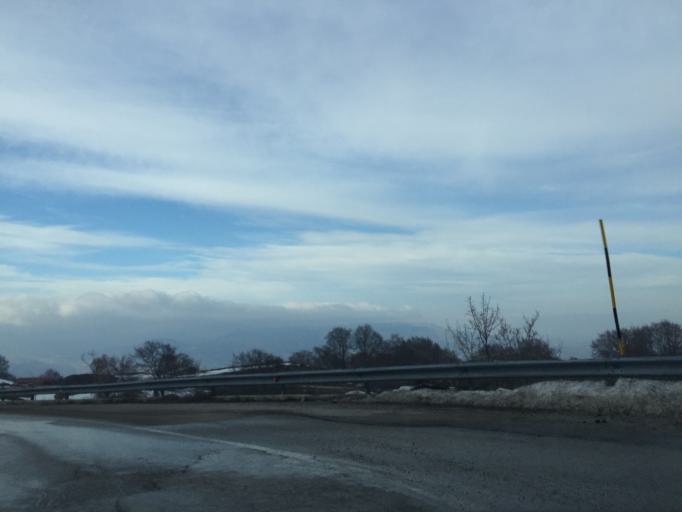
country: IT
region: Molise
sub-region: Provincia di Campobasso
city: San Massimo
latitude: 41.4652
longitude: 14.4160
